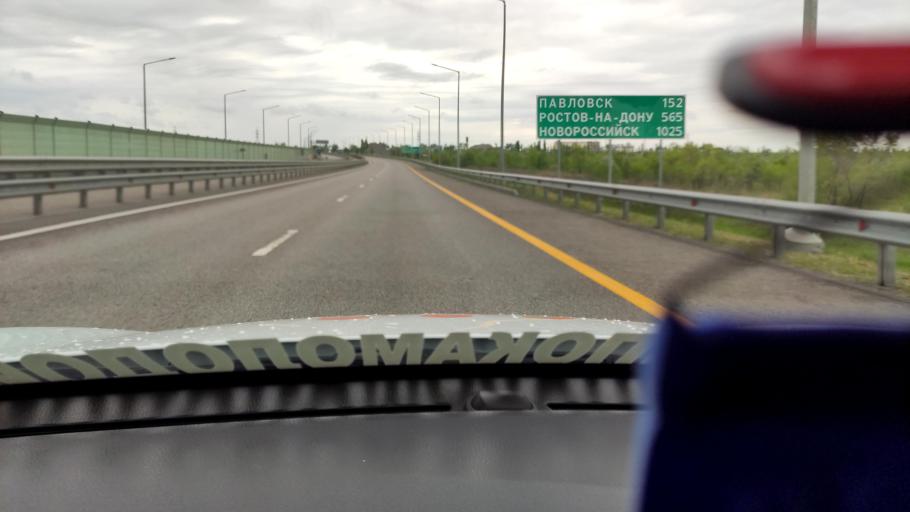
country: RU
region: Voronezj
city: Novaya Usman'
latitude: 51.6365
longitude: 39.3170
